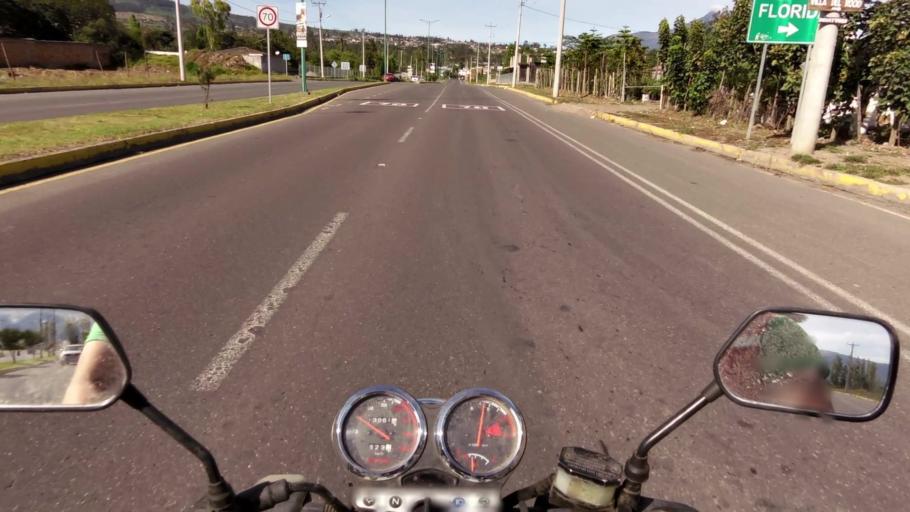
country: EC
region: Imbabura
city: Ibarra
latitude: 0.3321
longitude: -78.1477
